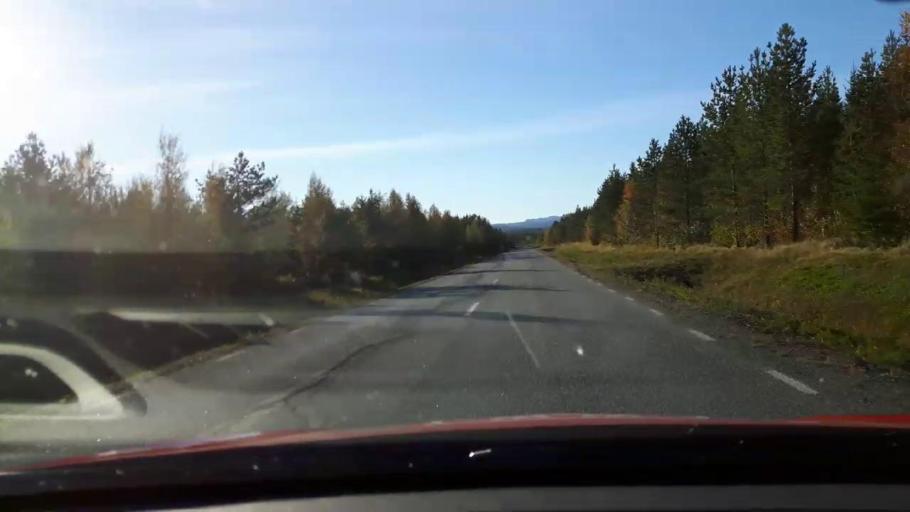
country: SE
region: Jaemtland
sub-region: OEstersunds Kommun
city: Lit
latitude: 63.8582
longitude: 14.9877
